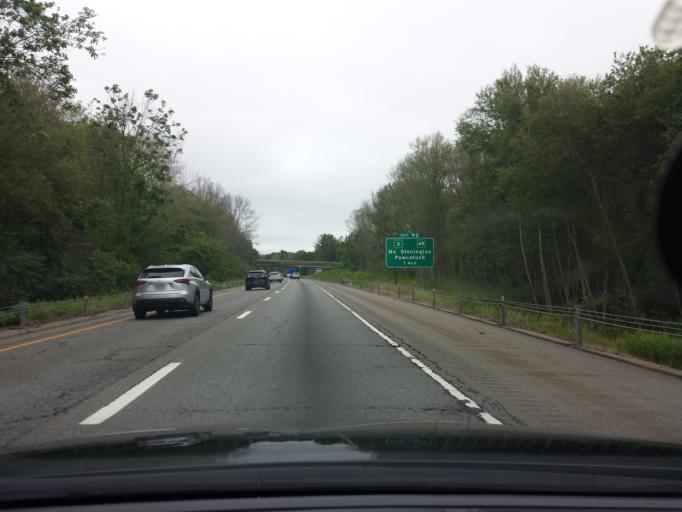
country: US
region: Connecticut
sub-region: New London County
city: Pawcatuck
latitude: 41.3939
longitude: -71.8702
